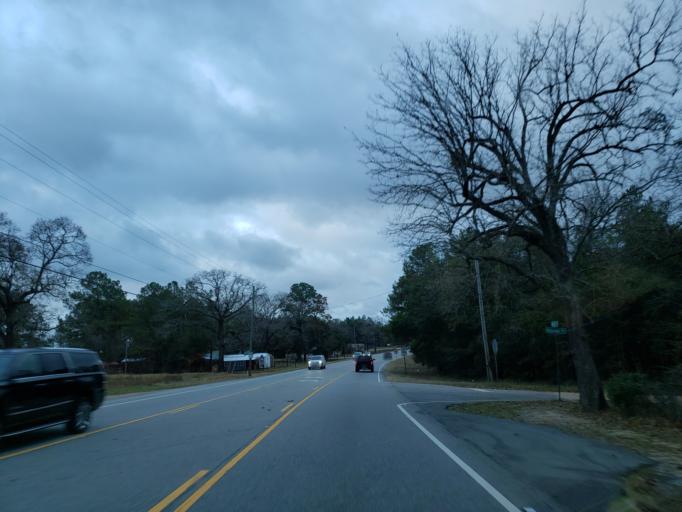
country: US
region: Mississippi
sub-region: George County
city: Lucedale
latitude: 30.8465
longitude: -88.3962
